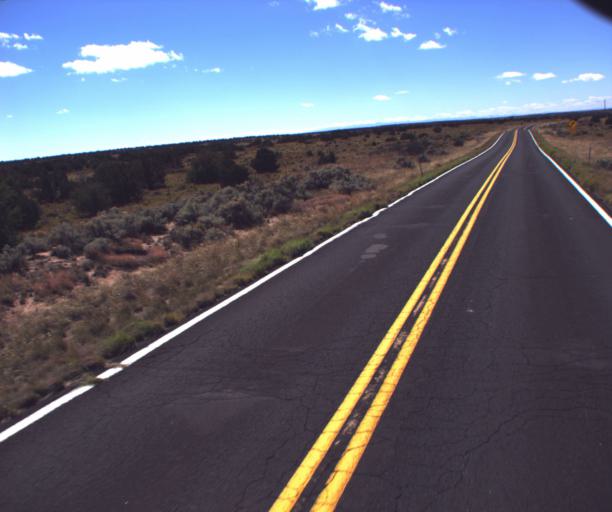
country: US
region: Arizona
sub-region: Apache County
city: Houck
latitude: 34.9578
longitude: -109.1591
